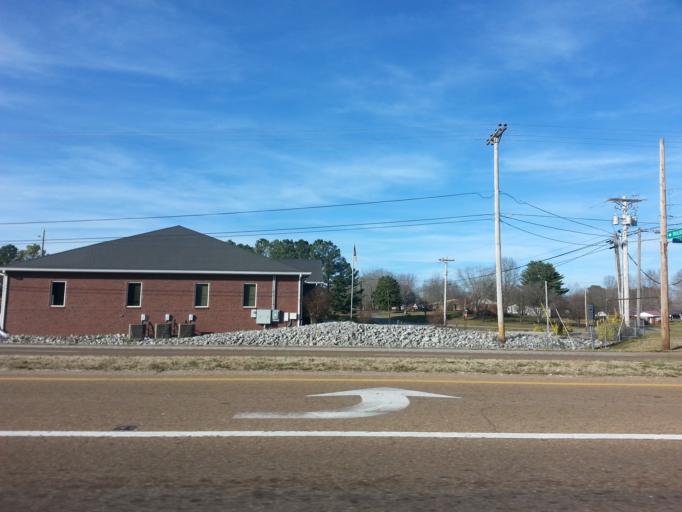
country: US
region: Tennessee
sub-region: Warren County
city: McMinnville
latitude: 35.6991
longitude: -85.7668
